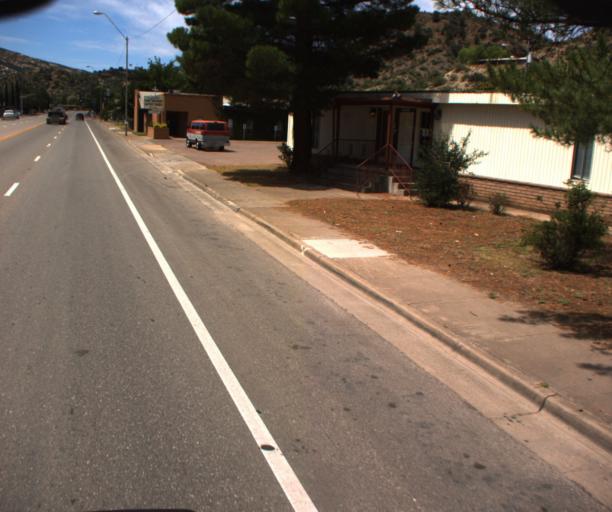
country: US
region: Arizona
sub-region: Gila County
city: Miami
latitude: 33.3965
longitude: -110.8740
